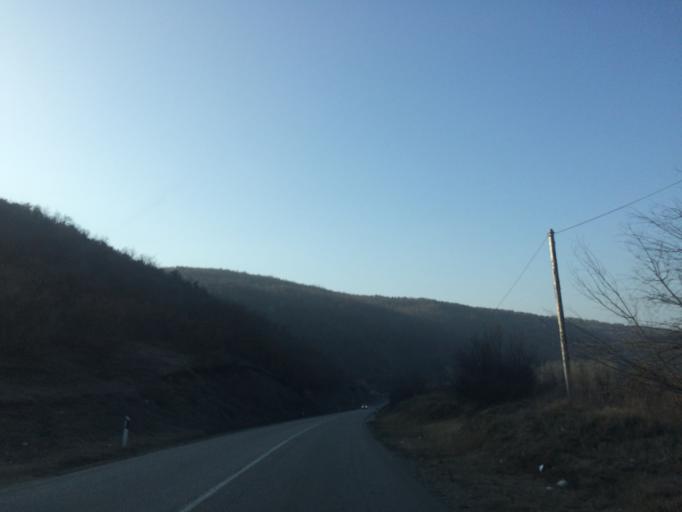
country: XK
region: Pec
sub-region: Komuna e Pejes
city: Kosuriq
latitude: 42.5084
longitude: 20.5453
